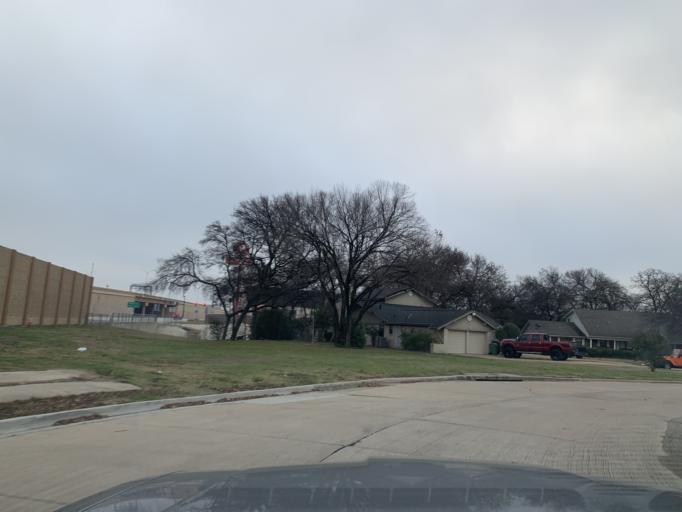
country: US
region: Texas
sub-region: Tarrant County
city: Bedford
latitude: 32.8391
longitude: -97.1532
